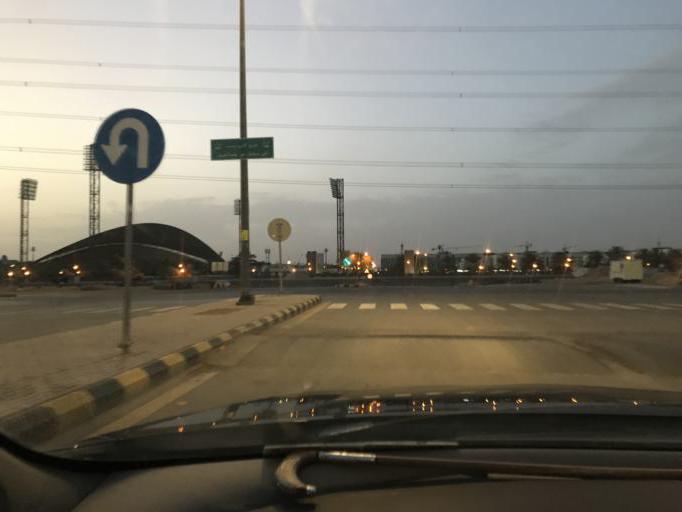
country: SA
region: Ar Riyad
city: Riyadh
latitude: 24.8040
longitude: 46.7061
